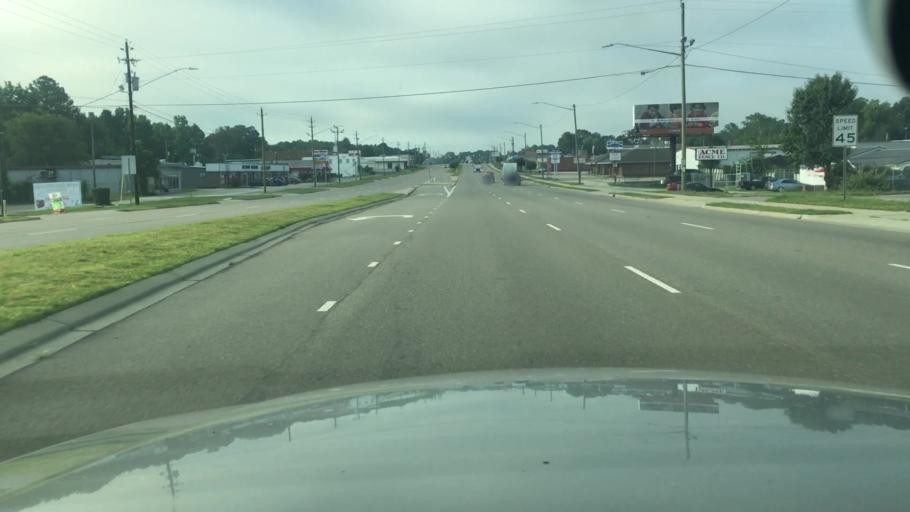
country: US
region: North Carolina
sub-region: Cumberland County
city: Fort Bragg
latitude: 35.0983
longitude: -78.9571
